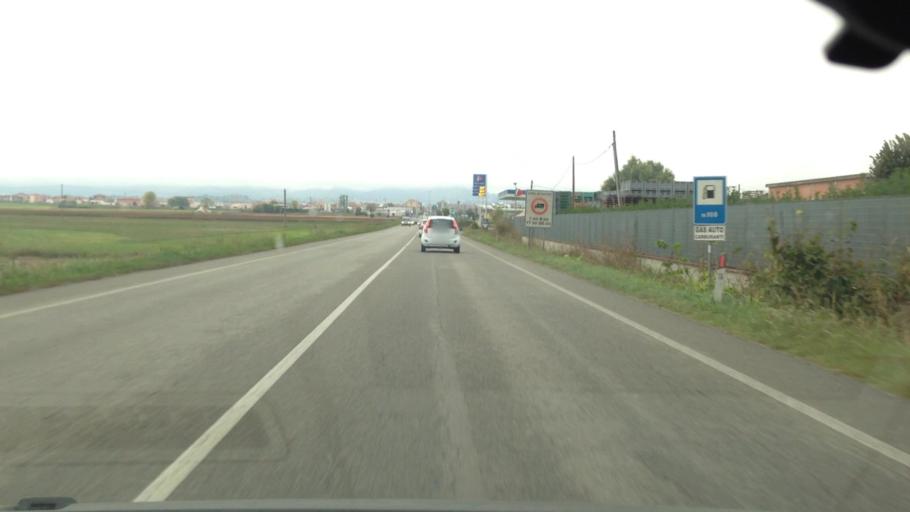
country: IT
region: Piedmont
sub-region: Provincia di Torino
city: Riva Presso Chieri
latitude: 44.9949
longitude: 7.8584
